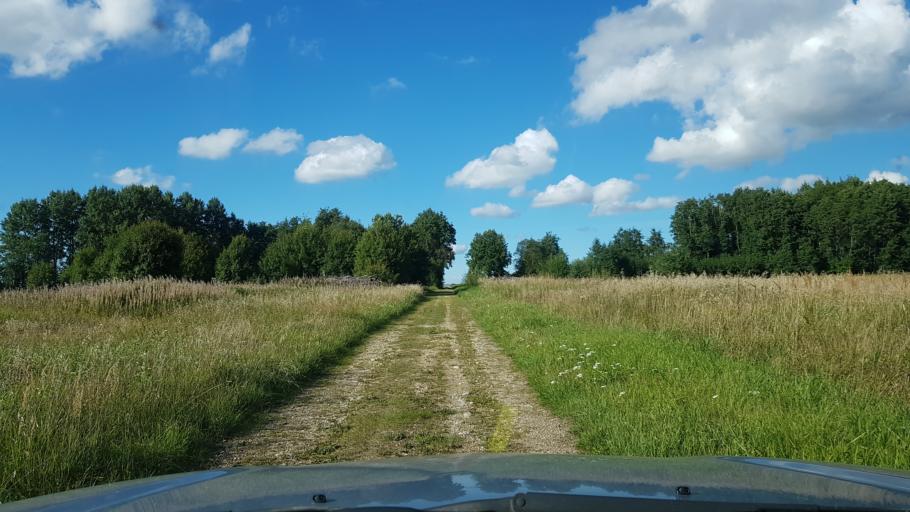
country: EE
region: Harju
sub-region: Kiili vald
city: Kiili
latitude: 59.3583
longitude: 24.8355
